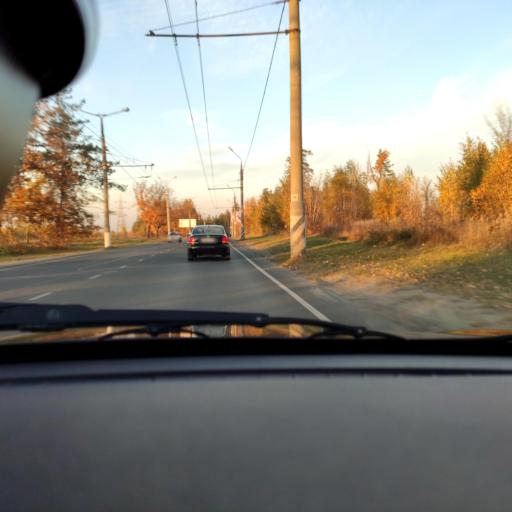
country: RU
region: Samara
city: Tol'yatti
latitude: 53.4866
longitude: 49.3821
